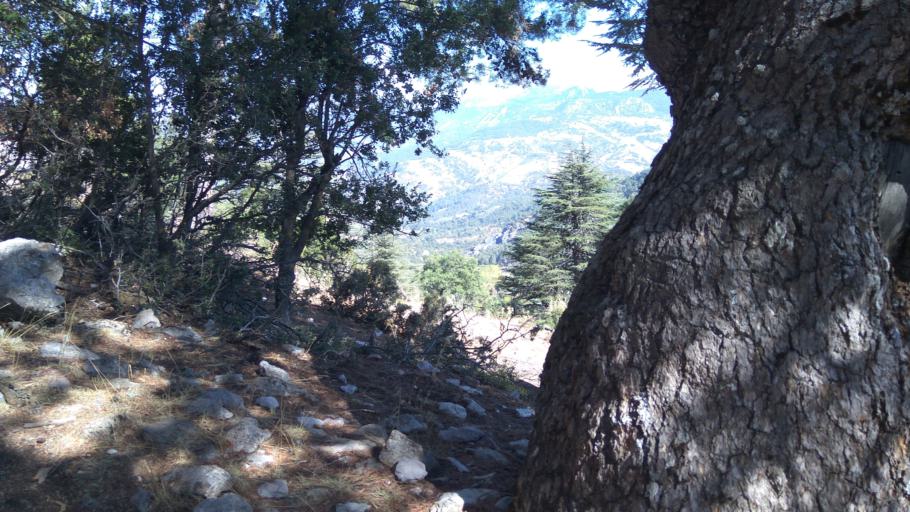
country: TR
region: Antalya
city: Altinyaka
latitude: 36.7129
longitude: 30.3653
